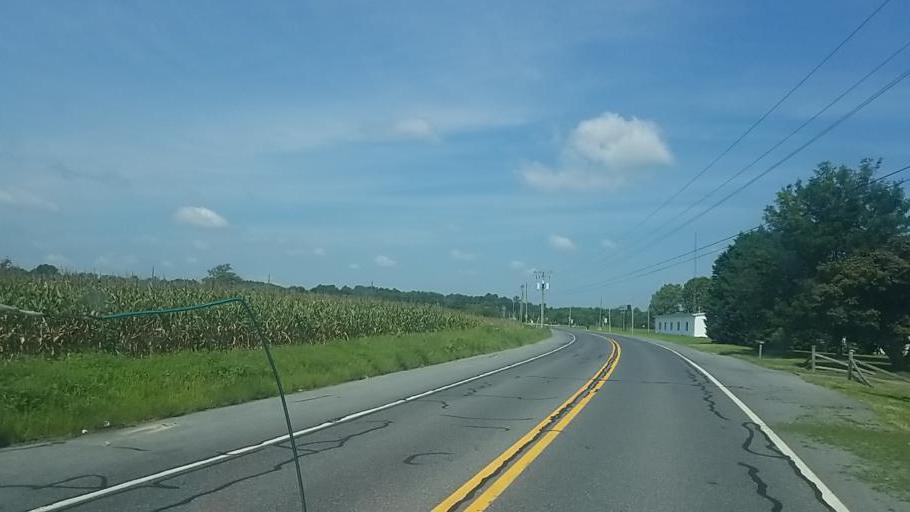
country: US
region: Delaware
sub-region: Sussex County
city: Seaford
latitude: 38.6836
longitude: -75.5877
